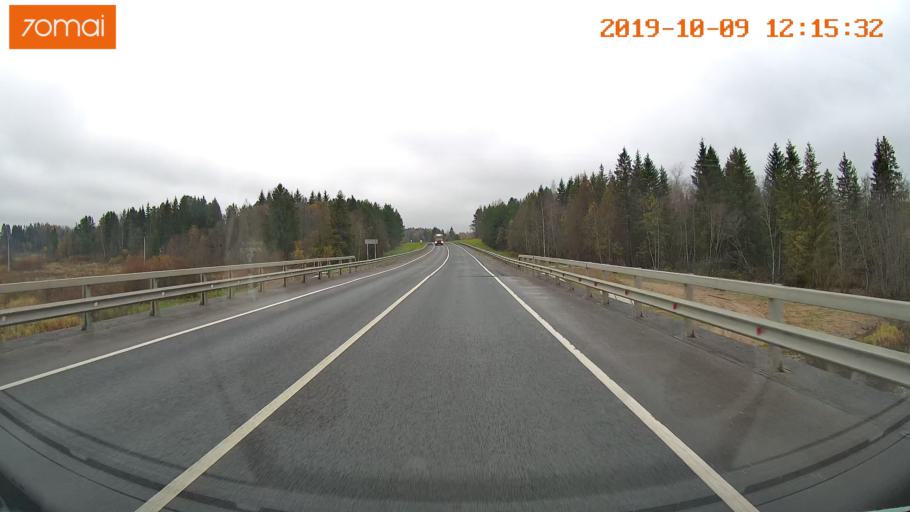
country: RU
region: Jaroslavl
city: Prechistoye
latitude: 58.4821
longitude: 40.3237
